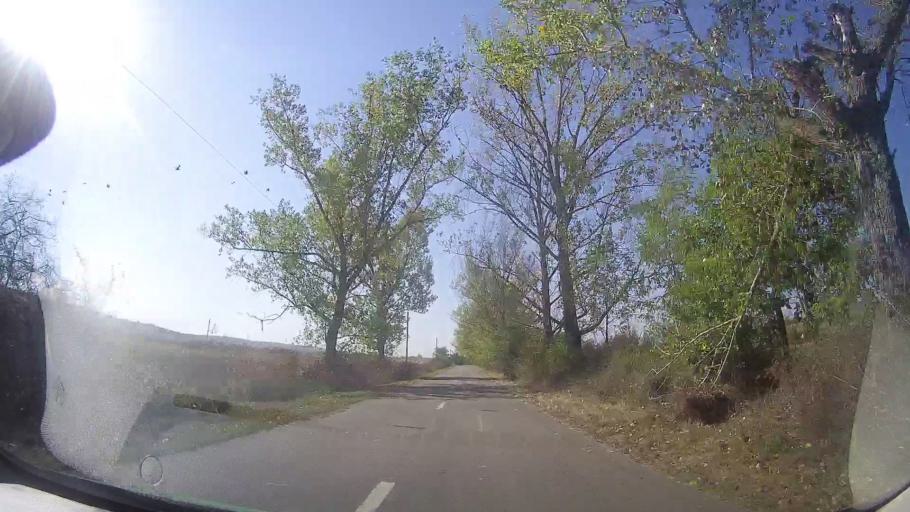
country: RO
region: Timis
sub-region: Comuna Secas
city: Secas
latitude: 45.8594
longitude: 21.8037
